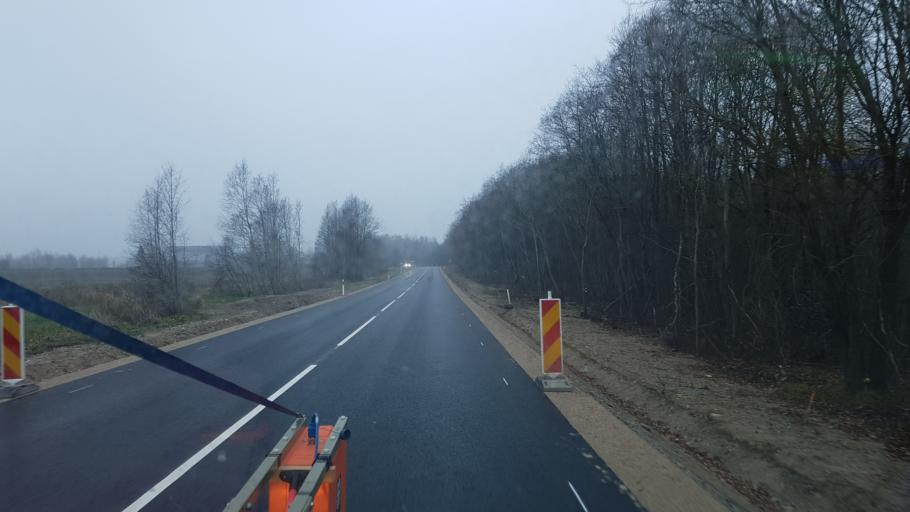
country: EE
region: Raplamaa
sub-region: Kohila vald
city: Kohila
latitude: 59.1775
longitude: 24.8144
